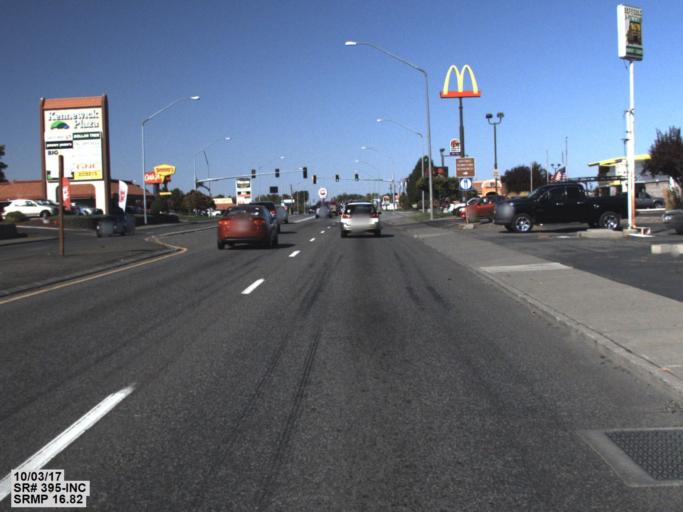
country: US
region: Washington
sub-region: Benton County
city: Kennewick
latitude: 46.2080
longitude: -119.1588
